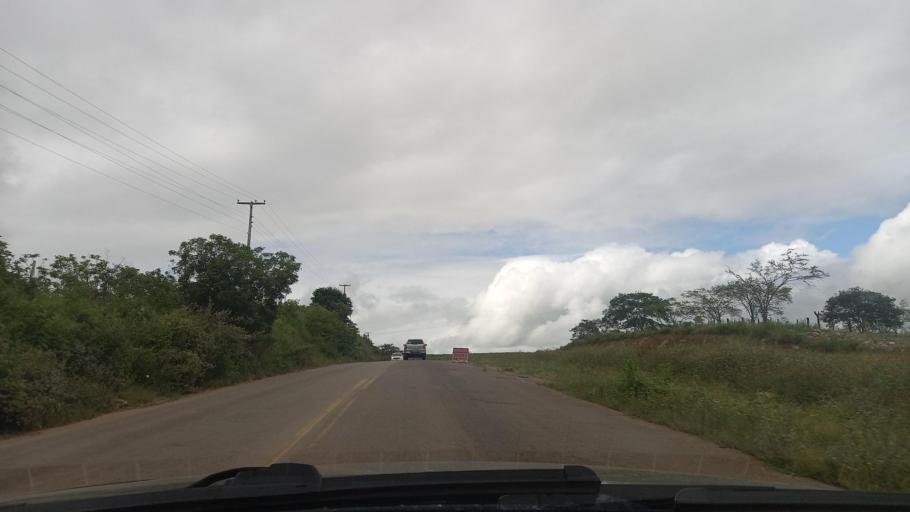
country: BR
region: Alagoas
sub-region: Batalha
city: Batalha
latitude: -9.6353
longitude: -37.1975
